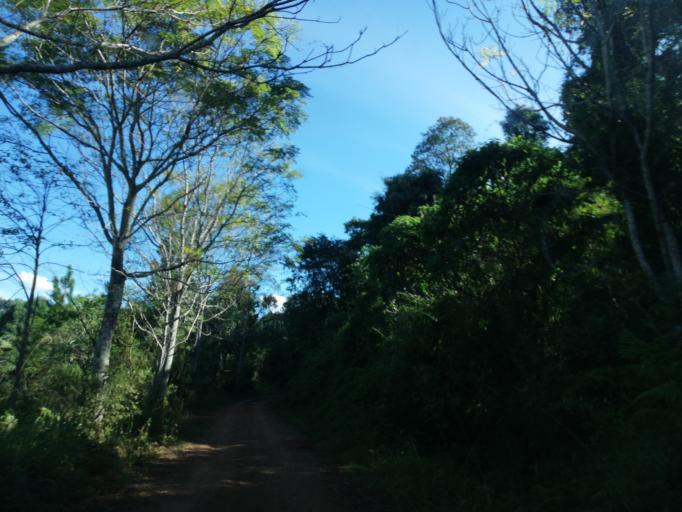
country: AR
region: Misiones
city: Dos de Mayo
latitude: -27.0155
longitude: -54.4370
